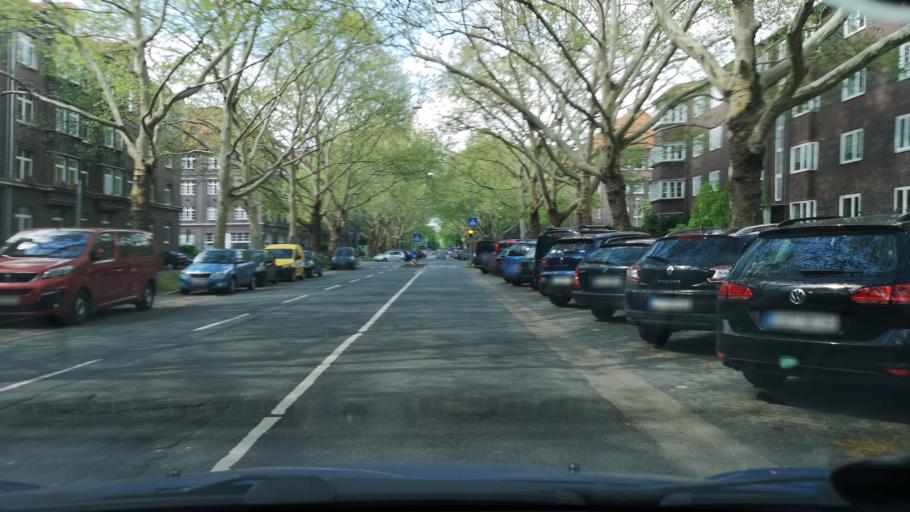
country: DE
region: Lower Saxony
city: Hannover
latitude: 52.3572
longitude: 9.7627
